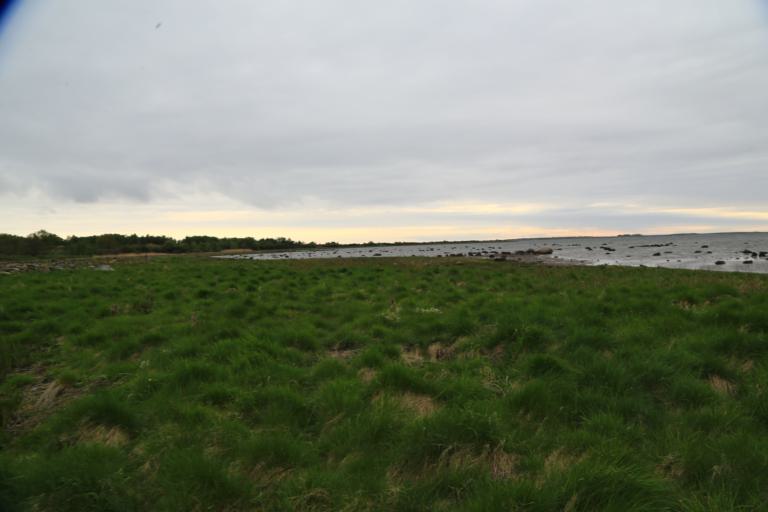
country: SE
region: Halland
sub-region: Varbergs Kommun
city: Varberg
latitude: 57.1535
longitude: 12.2247
